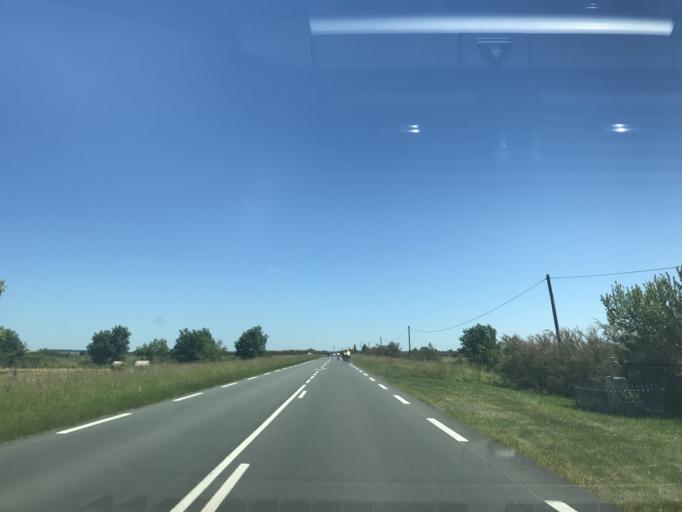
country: FR
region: Poitou-Charentes
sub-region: Departement de la Charente-Maritime
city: Meschers-sur-Gironde
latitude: 45.5615
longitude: -0.9348
